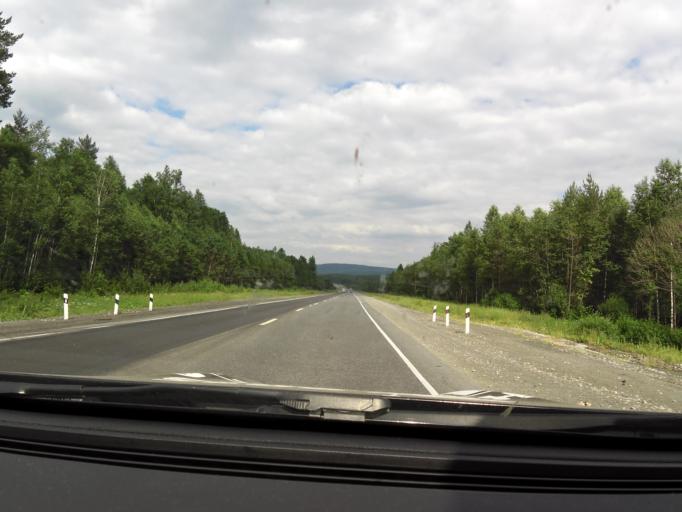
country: RU
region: Sverdlovsk
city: Druzhinino
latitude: 56.8294
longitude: 59.6087
